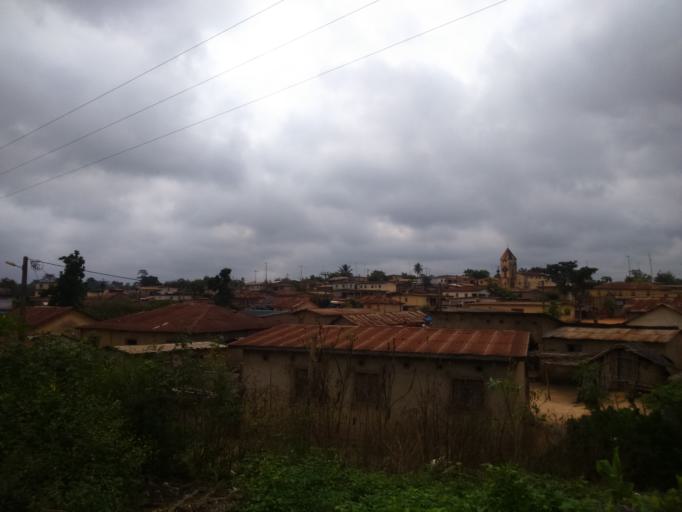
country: CI
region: Lagunes
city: Agou
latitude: 6.0569
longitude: -4.0965
